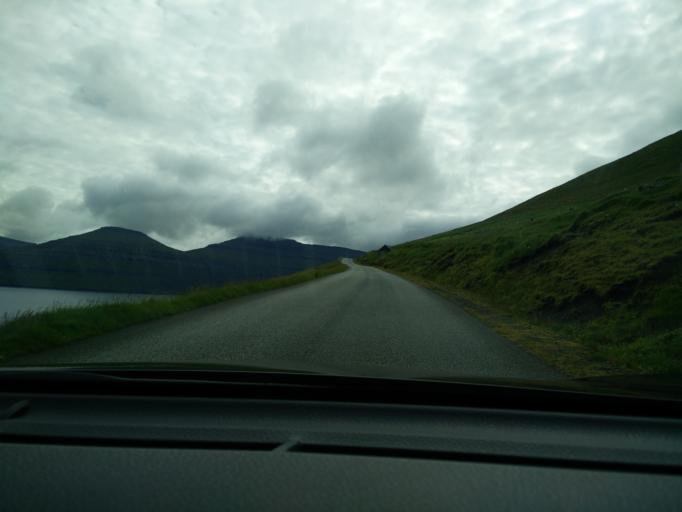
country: FO
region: Eysturoy
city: Eystur
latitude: 62.2079
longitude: -6.6948
